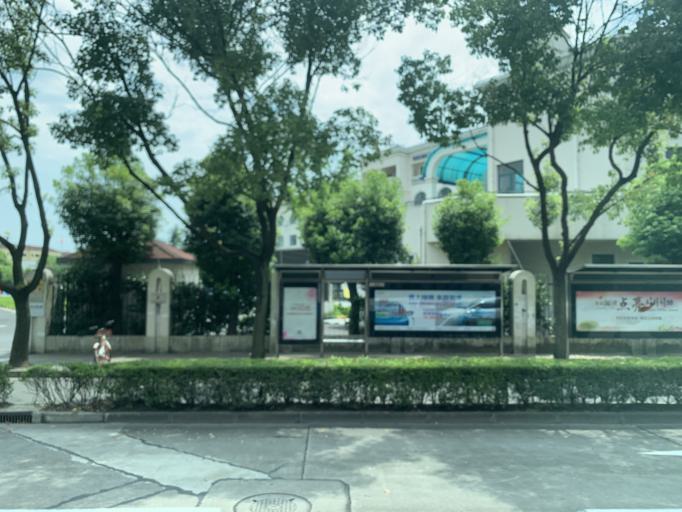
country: CN
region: Shanghai Shi
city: Huamu
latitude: 31.2507
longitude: 121.5789
